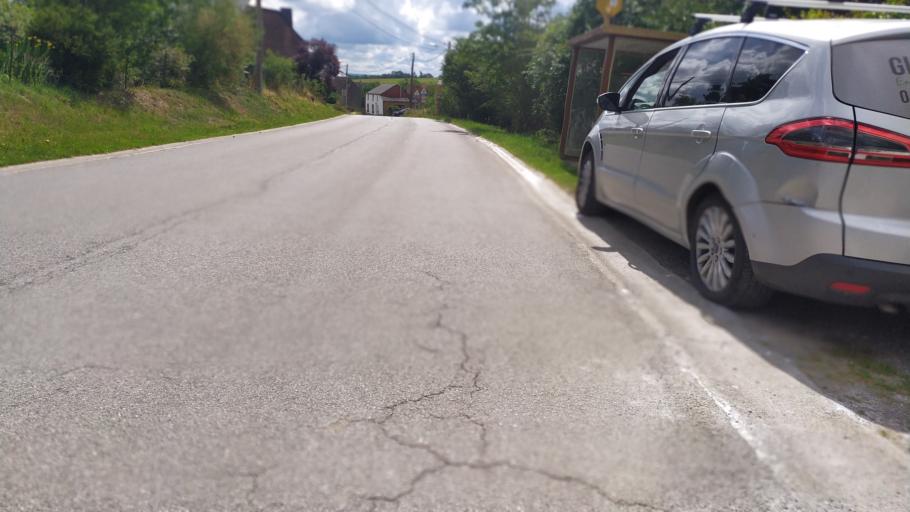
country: BE
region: Wallonia
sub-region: Province de Namur
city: Houyet
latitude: 50.1617
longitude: 5.0391
